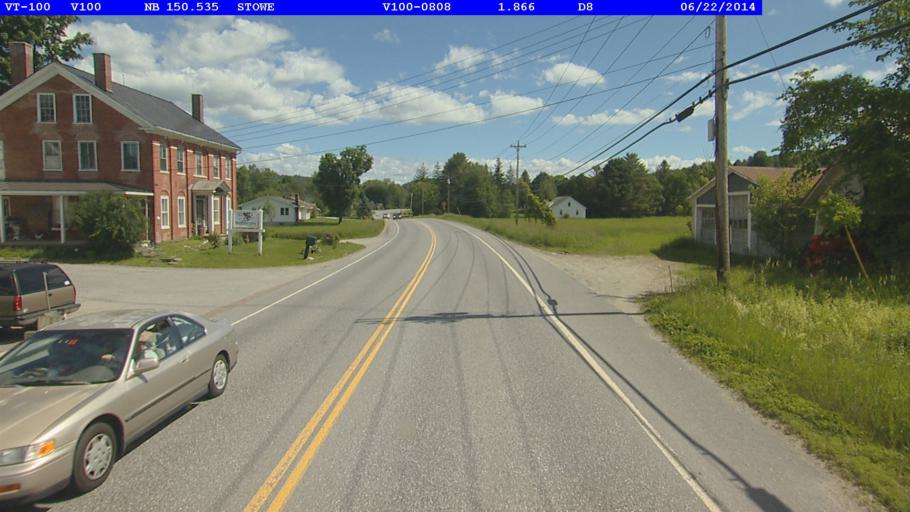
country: US
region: Vermont
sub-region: Washington County
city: Waterbury
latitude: 44.4473
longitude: -72.7004
